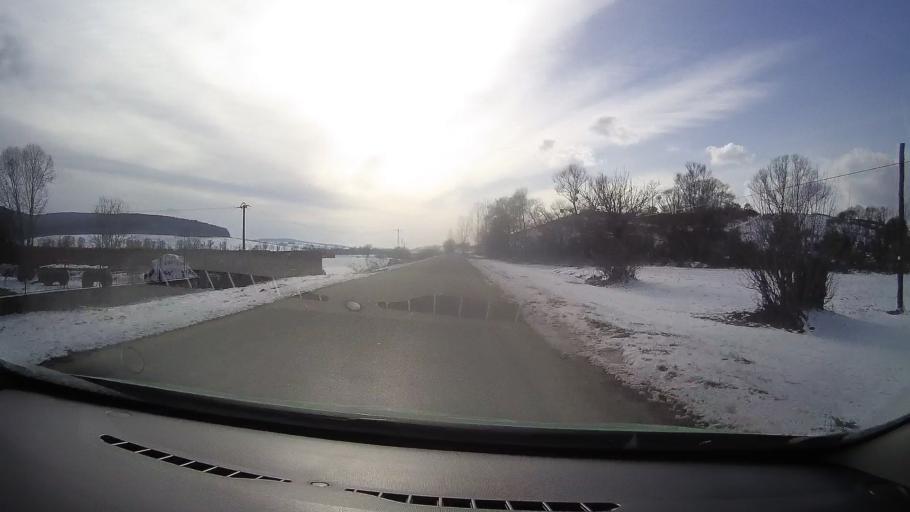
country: RO
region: Sibiu
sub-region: Comuna Iacobeni
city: Iacobeni
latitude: 46.0395
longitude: 24.7300
